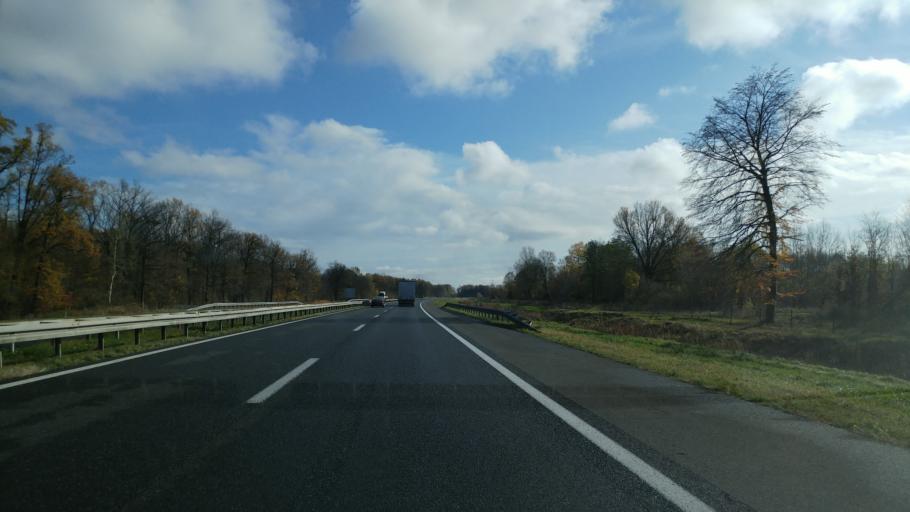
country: HR
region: Zagrebacka
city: Lupoglav
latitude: 45.7468
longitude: 16.3155
